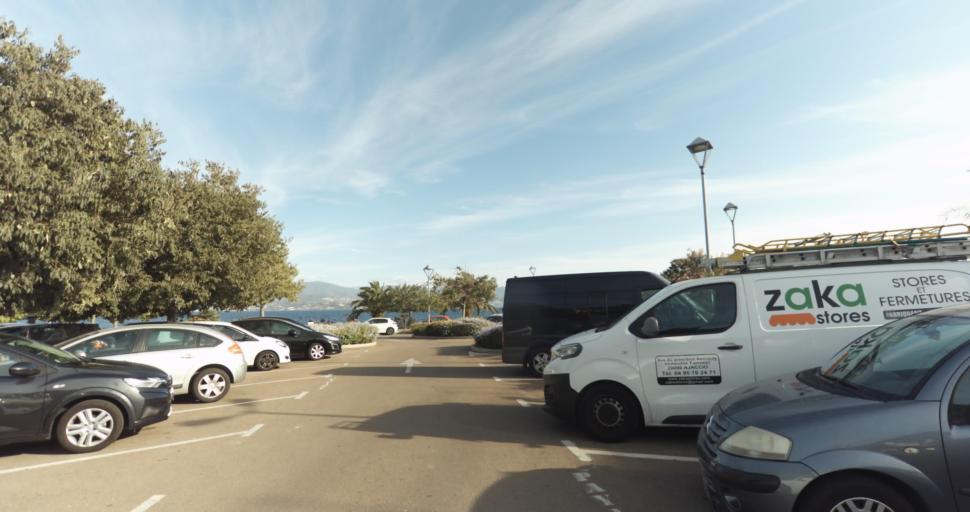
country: FR
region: Corsica
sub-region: Departement de la Corse-du-Sud
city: Ajaccio
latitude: 41.9133
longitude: 8.7292
